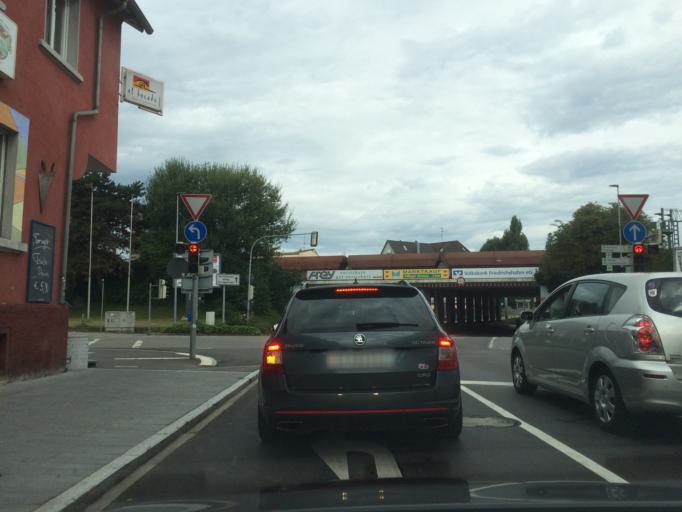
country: DE
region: Baden-Wuerttemberg
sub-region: Tuebingen Region
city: Friedrichshafen
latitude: 47.6534
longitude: 9.4824
